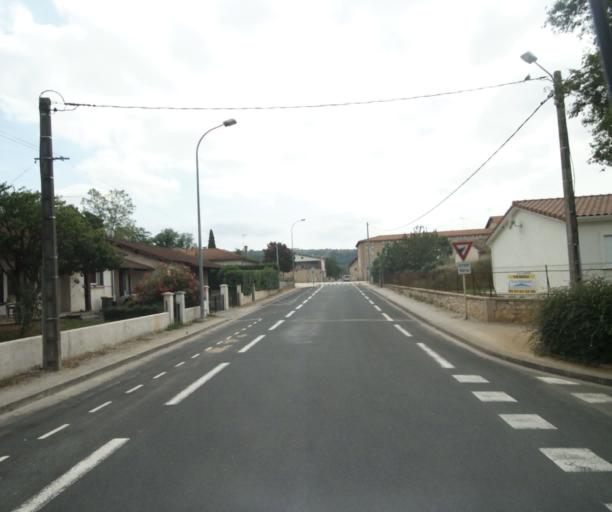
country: FR
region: Midi-Pyrenees
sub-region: Departement de la Haute-Garonne
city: Revel
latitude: 43.4567
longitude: 2.0128
